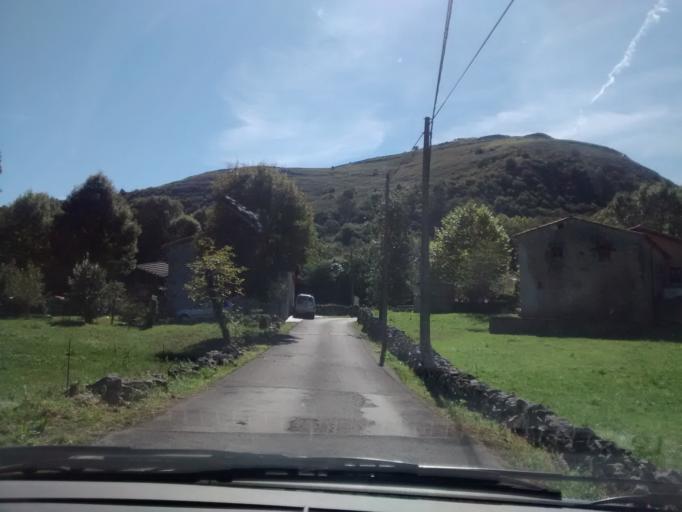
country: ES
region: Cantabria
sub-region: Provincia de Cantabria
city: Entrambasaguas
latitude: 43.3424
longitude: -3.6927
